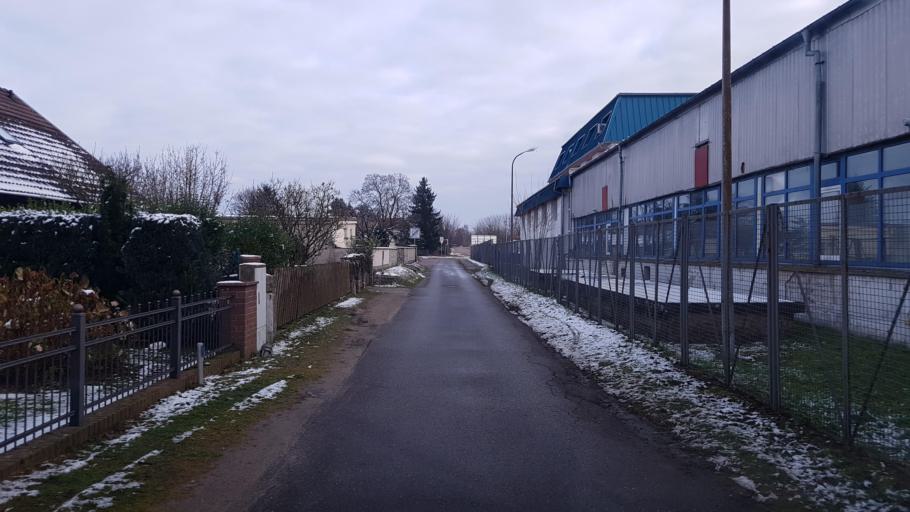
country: DE
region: Brandenburg
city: Strausberg
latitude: 52.5709
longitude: 13.8929
